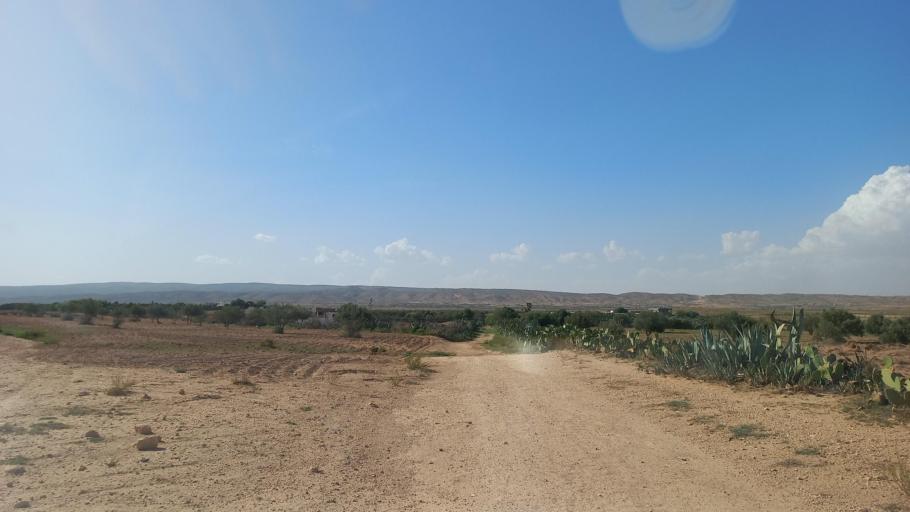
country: TN
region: Al Qasrayn
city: Kasserine
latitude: 35.3138
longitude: 9.0151
